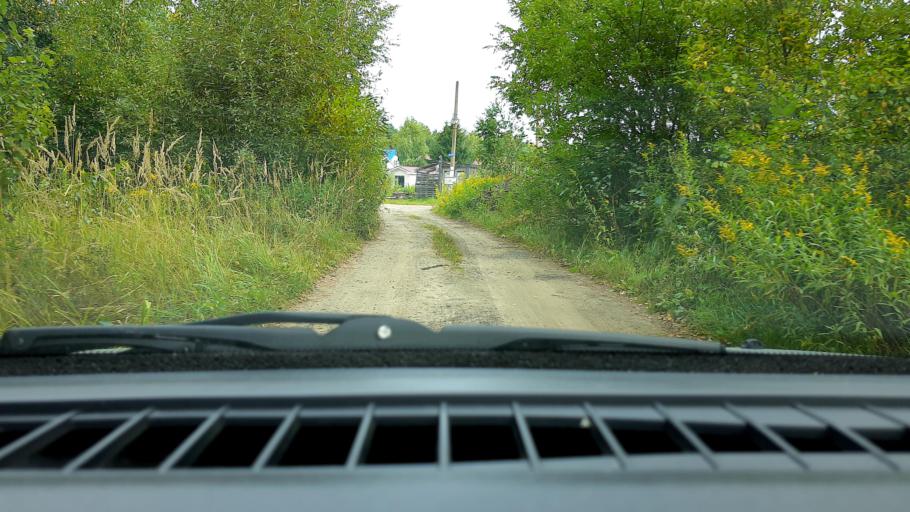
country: RU
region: Nizjnij Novgorod
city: Gorbatovka
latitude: 56.3251
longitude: 43.6933
